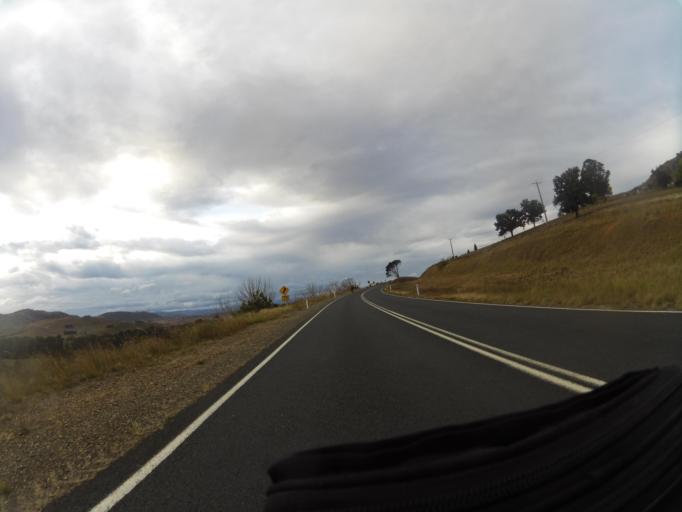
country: AU
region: New South Wales
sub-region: Snowy River
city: Jindabyne
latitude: -36.0838
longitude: 147.9776
